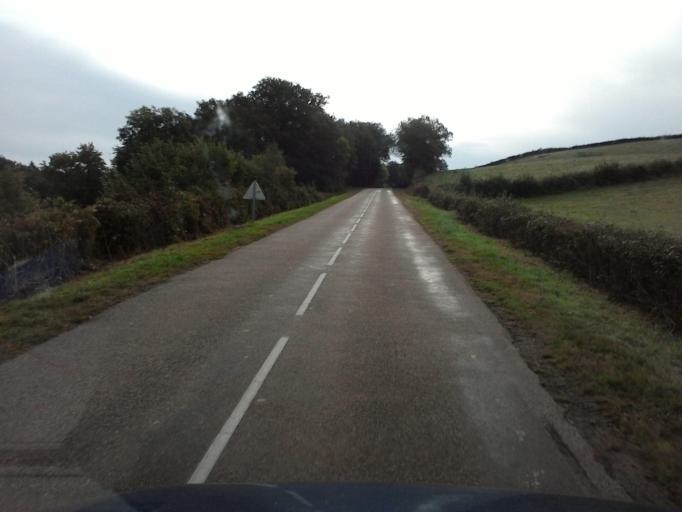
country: FR
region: Bourgogne
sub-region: Departement de la Nievre
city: Lormes
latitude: 47.2264
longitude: 3.8302
